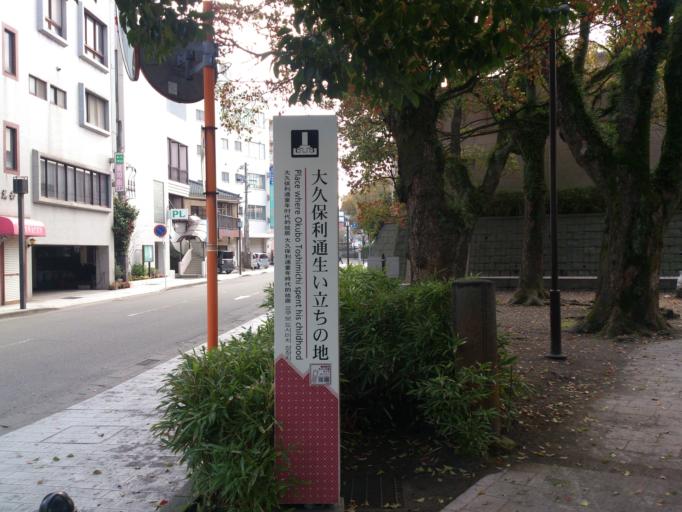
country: JP
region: Kagoshima
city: Kagoshima-shi
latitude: 31.5850
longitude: 130.5475
